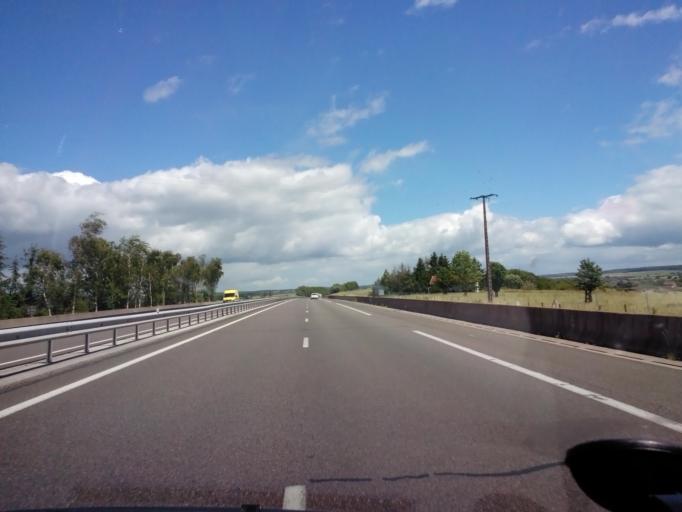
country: FR
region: Lorraine
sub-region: Departement des Vosges
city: Bulgneville
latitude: 48.1848
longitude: 5.7535
